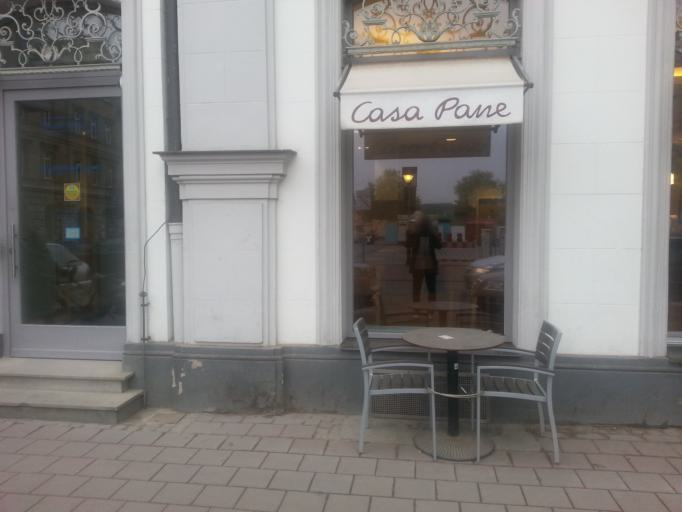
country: DE
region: Bavaria
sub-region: Regierungsbezirk Mittelfranken
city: Furth
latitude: 49.4729
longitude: 10.9904
